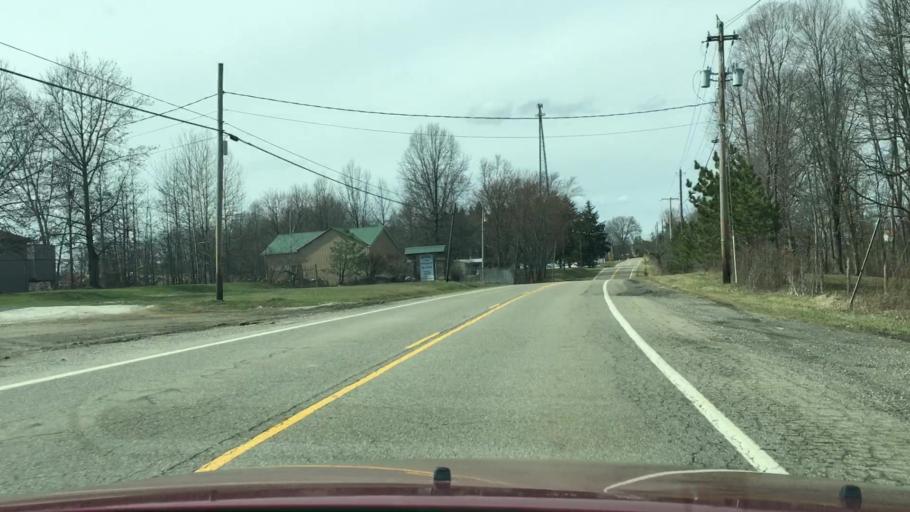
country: US
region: Ohio
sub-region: Mahoning County
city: Sebring
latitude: 41.0107
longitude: -81.0469
